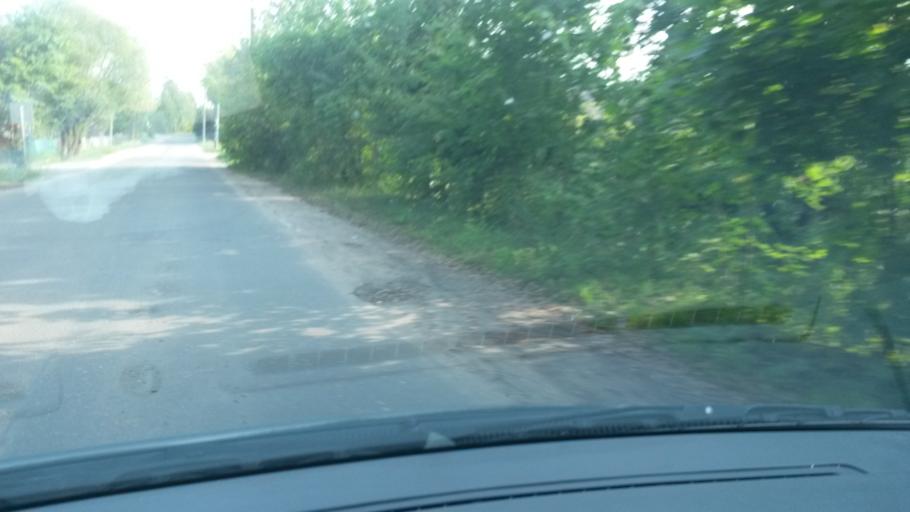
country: RU
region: Jaroslavl
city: Petrovsk
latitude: 57.0079
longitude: 39.2705
